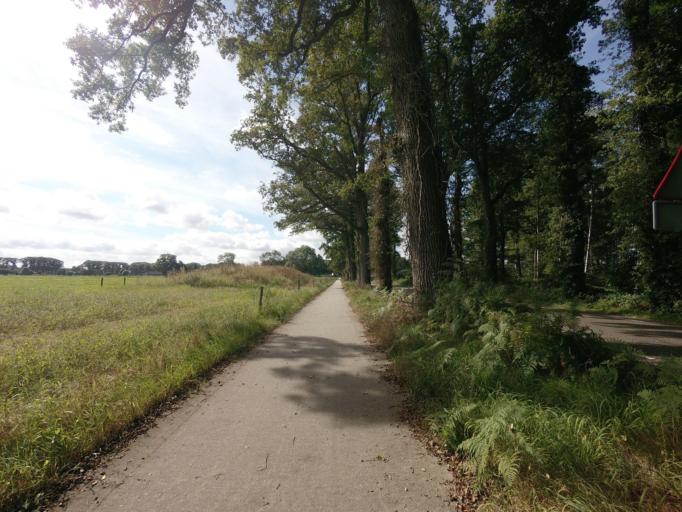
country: NL
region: Overijssel
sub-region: Gemeente Olst-Wijhe
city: Boskamp
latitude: 52.3196
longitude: 6.1715
